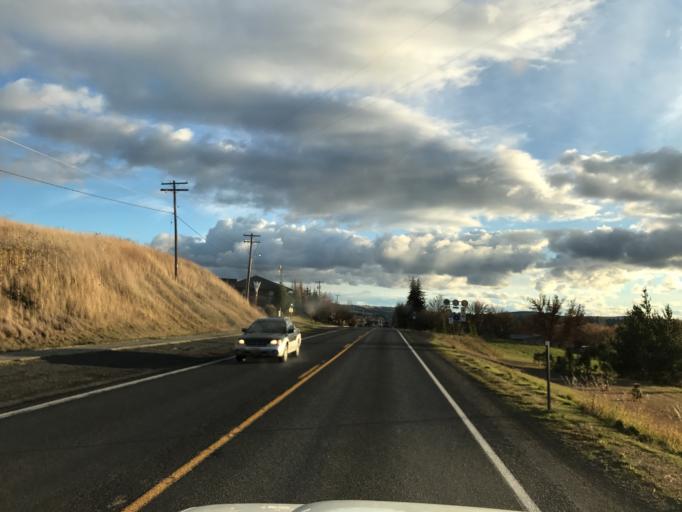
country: US
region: Idaho
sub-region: Latah County
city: Moscow
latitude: 46.7484
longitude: -117.0016
